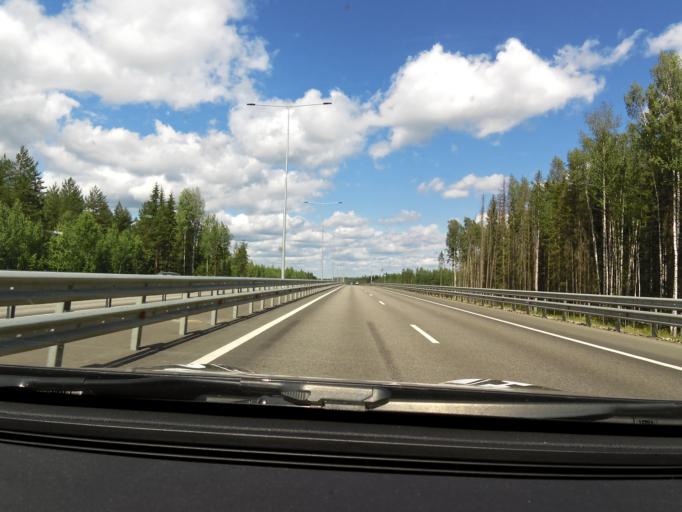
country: RU
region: Tverskaya
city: Vyshniy Volochek
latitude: 57.3983
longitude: 34.5394
